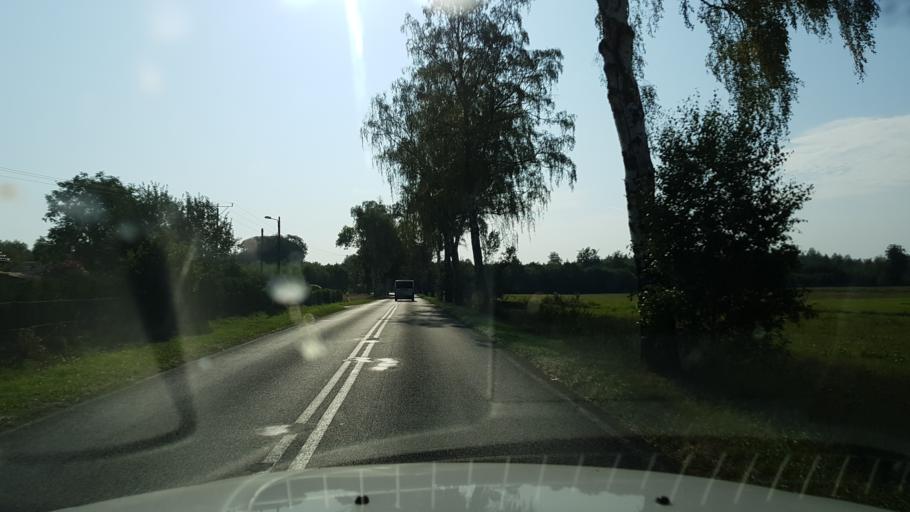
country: PL
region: West Pomeranian Voivodeship
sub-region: Powiat gryficki
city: Ploty
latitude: 53.7825
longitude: 15.3323
